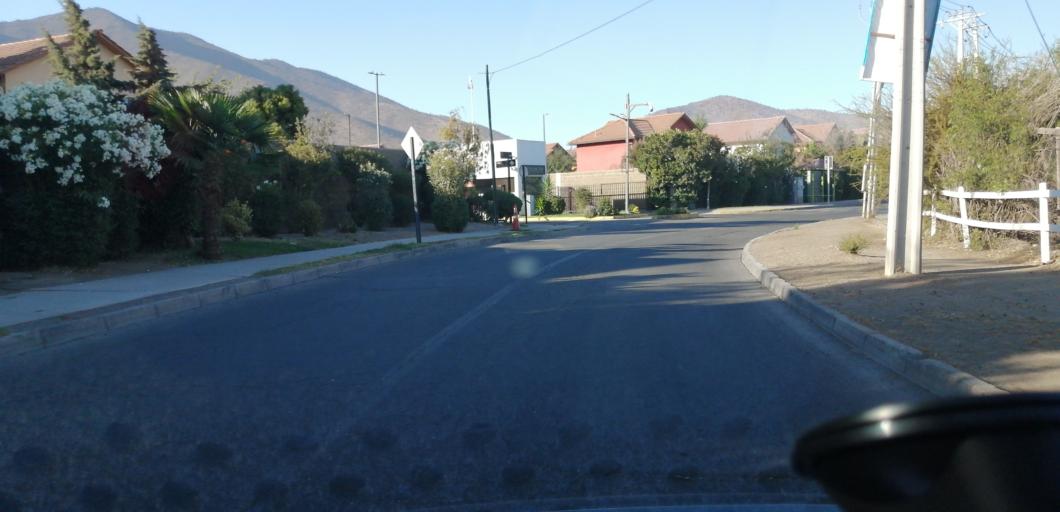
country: CL
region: Santiago Metropolitan
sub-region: Provincia de Santiago
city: Lo Prado
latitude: -33.4591
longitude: -70.8552
